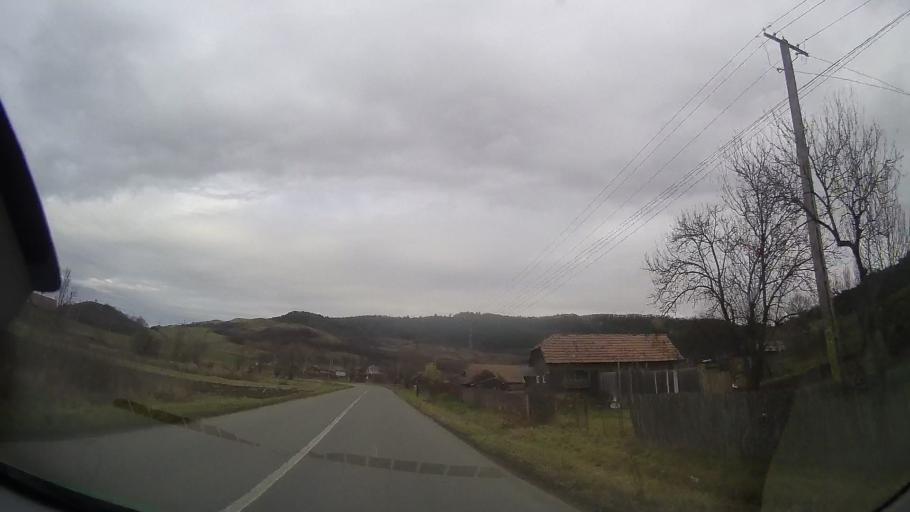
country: RO
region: Mures
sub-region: Comuna Faragau
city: Faragau
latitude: 46.7336
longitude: 24.5446
